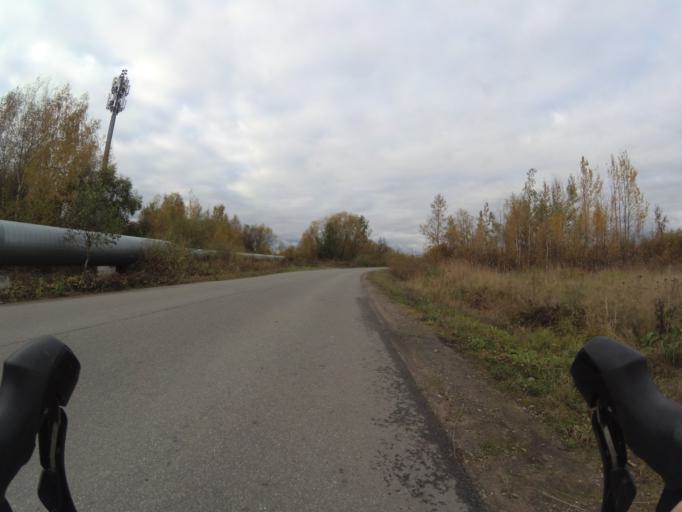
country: RU
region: St.-Petersburg
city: Lakhtinskiy
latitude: 60.0012
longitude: 30.1550
